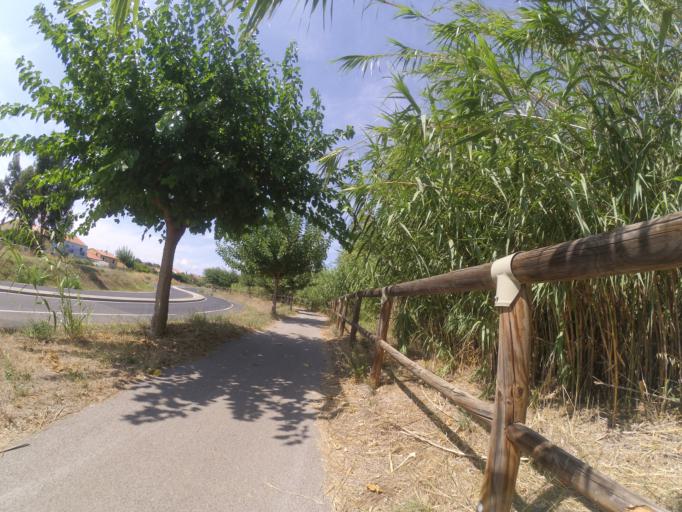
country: FR
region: Languedoc-Roussillon
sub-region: Departement des Pyrenees-Orientales
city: Peyrestortes
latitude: 42.7558
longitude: 2.8441
